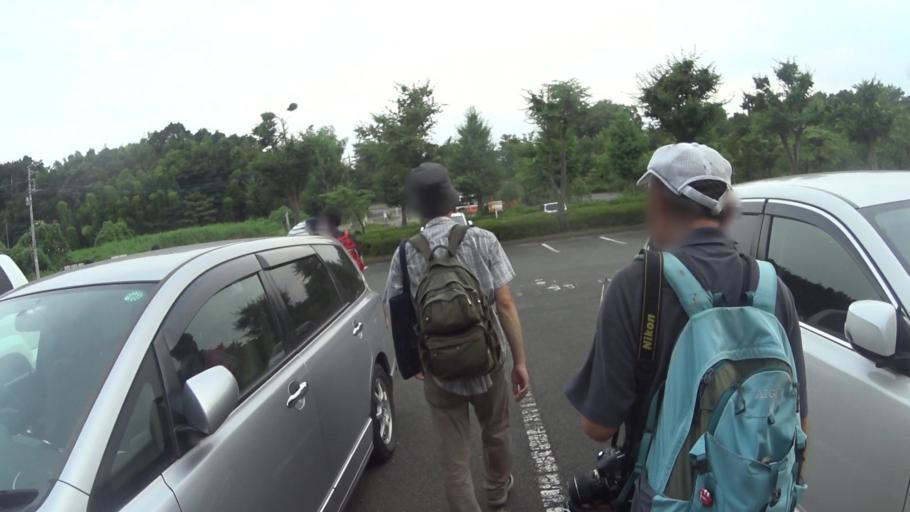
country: JP
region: Saitama
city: Okegawa
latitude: 35.9538
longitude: 139.5492
